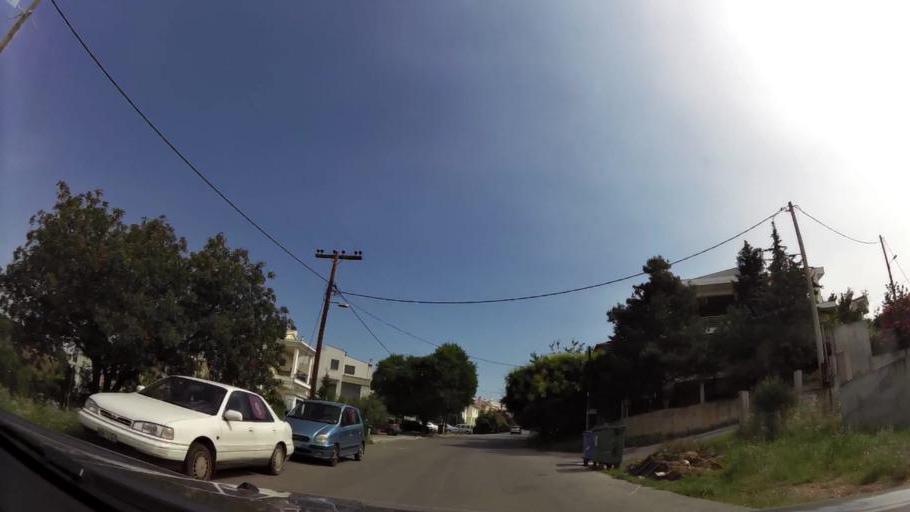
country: GR
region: Central Macedonia
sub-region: Nomos Thessalonikis
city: Panorama
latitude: 40.5791
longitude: 23.0065
